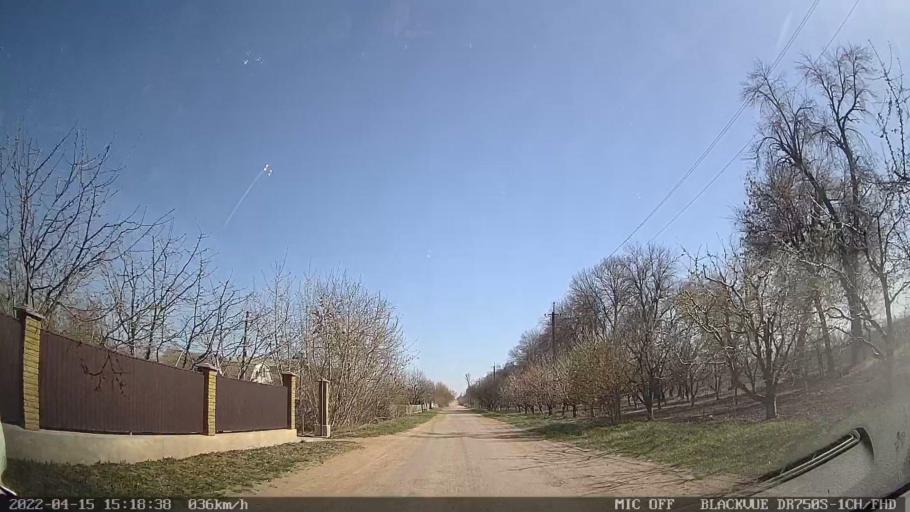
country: MD
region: Raionul Ocnita
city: Otaci
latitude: 48.3898
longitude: 27.9035
